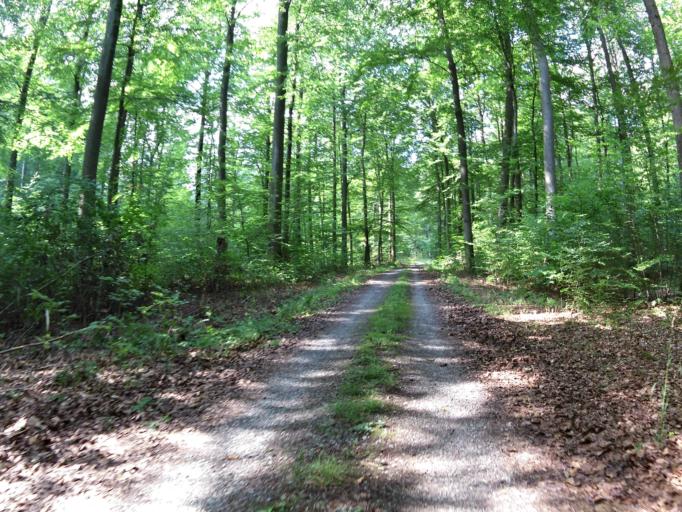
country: DE
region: Bavaria
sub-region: Regierungsbezirk Unterfranken
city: Kleinrinderfeld
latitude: 49.7083
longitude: 9.8210
